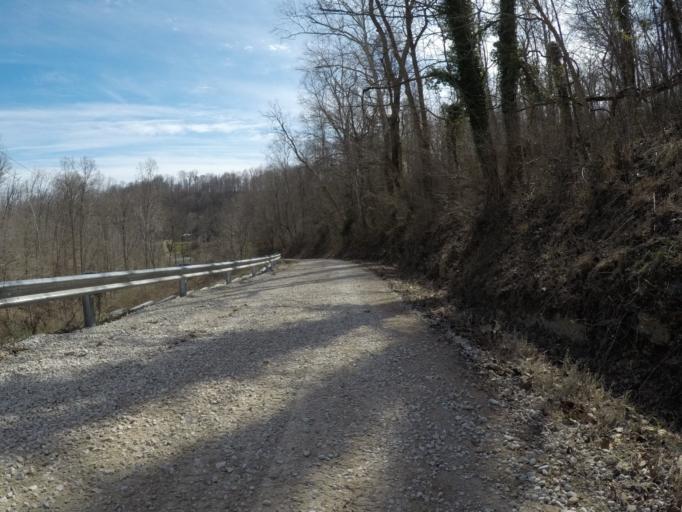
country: US
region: West Virginia
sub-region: Wayne County
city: Ceredo
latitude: 38.3473
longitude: -82.5483
